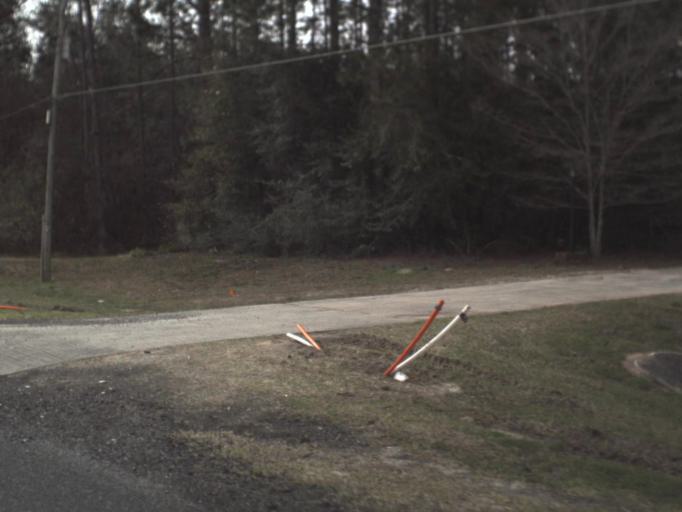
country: US
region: Florida
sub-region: Bay County
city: Youngstown
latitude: 30.2960
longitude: -85.4907
